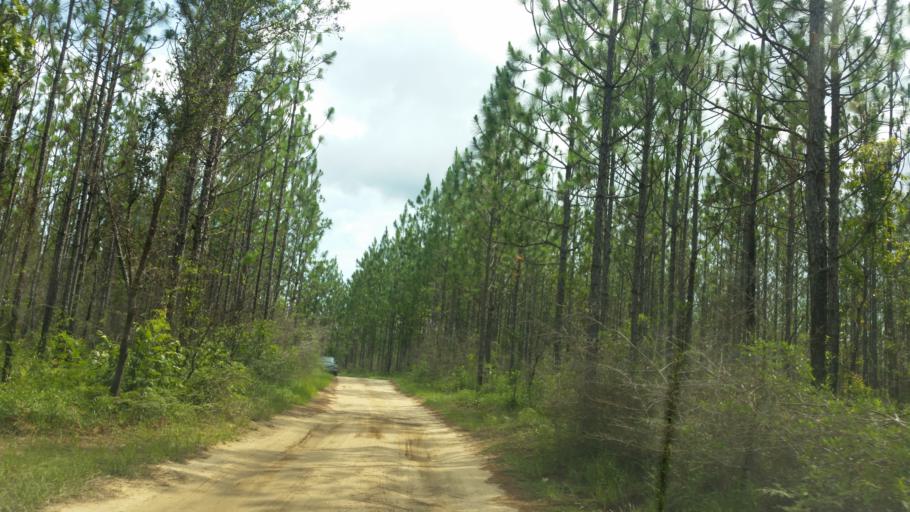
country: US
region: Florida
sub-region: Escambia County
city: Cantonment
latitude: 30.6359
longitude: -87.3895
